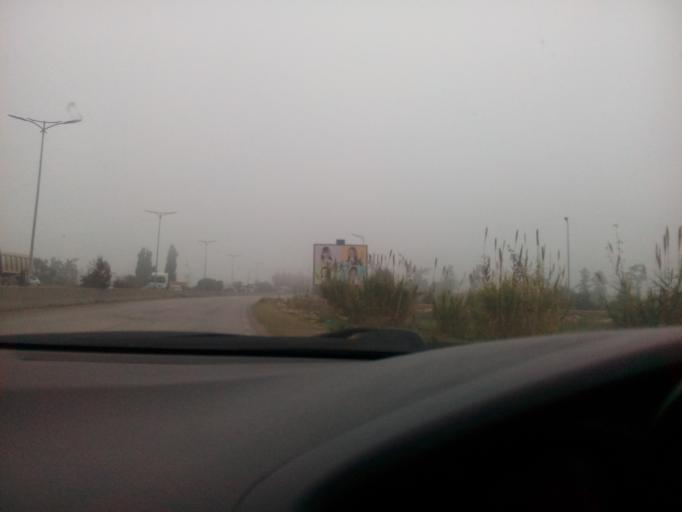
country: DZ
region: Oran
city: Bou Tlelis
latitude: 35.5726
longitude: -0.8797
